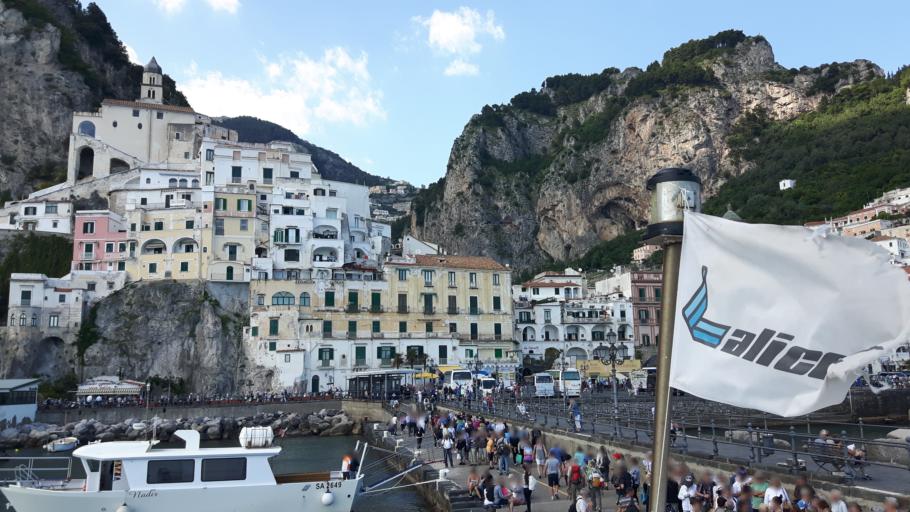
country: IT
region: Campania
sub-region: Provincia di Salerno
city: Amalfi
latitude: 40.6324
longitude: 14.6013
